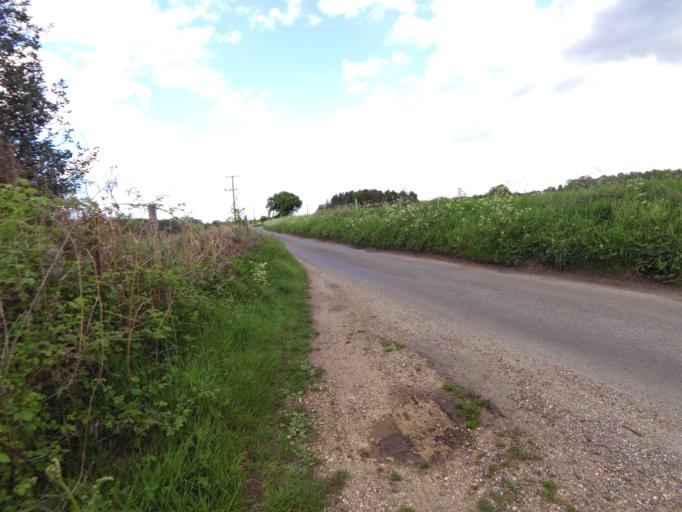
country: GB
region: England
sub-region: Suffolk
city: Elmswell
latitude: 52.2049
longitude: 0.9329
